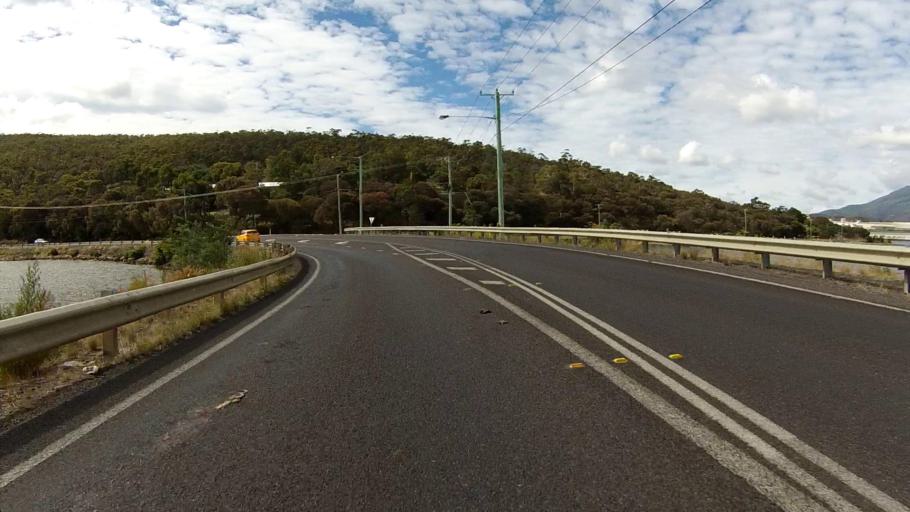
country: AU
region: Tasmania
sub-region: Glenorchy
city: Lutana
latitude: -42.8174
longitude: 147.3205
